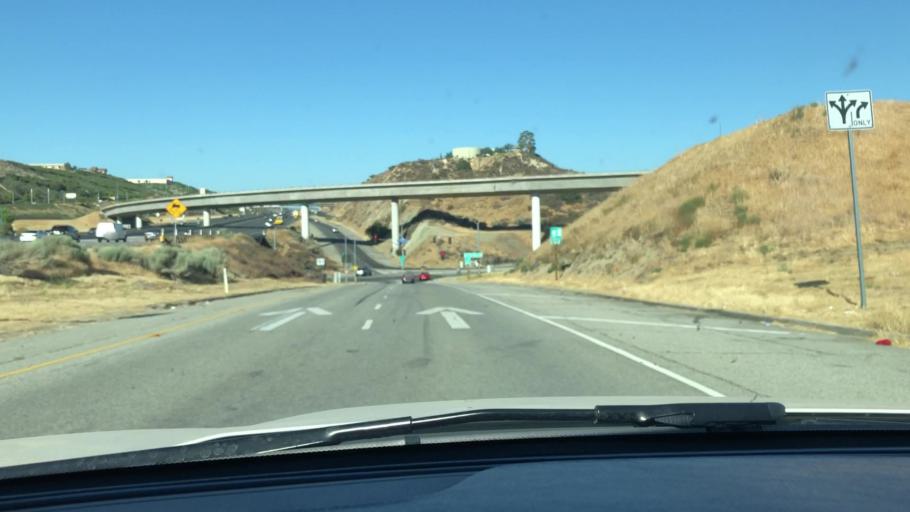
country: US
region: California
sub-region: Los Angeles County
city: Santa Clarita
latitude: 34.4035
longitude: -118.4540
